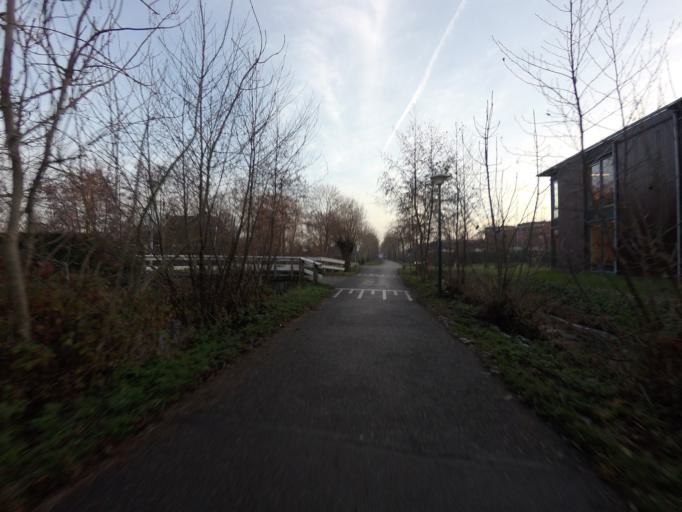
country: NL
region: Utrecht
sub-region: Gemeente Woerden
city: Woerden
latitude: 52.0836
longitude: 4.9105
